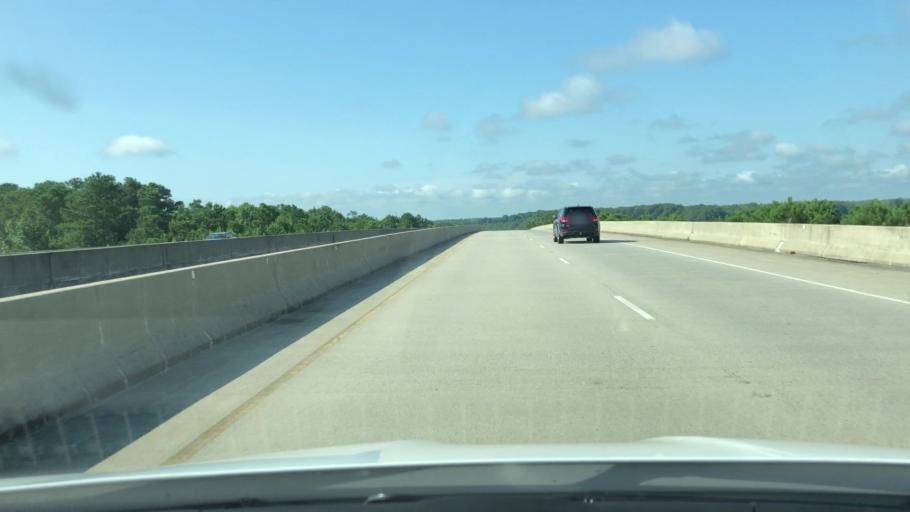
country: US
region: North Carolina
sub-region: Currituck County
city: Moyock
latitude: 36.4580
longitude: -76.3328
